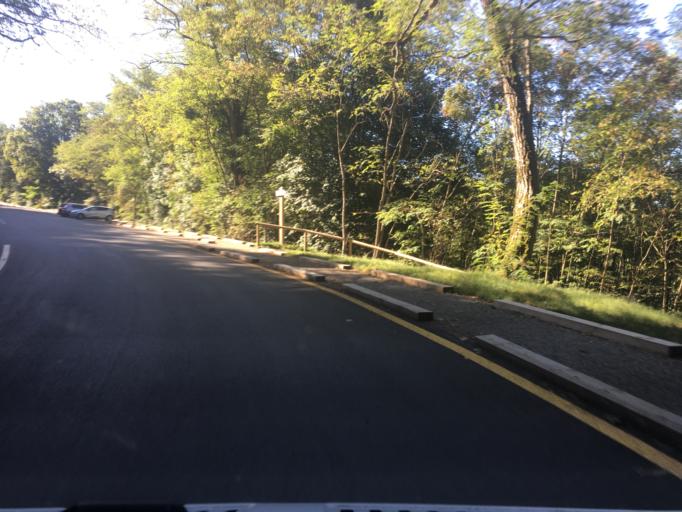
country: FR
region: Auvergne
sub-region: Departement du Cantal
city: Lanobre
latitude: 45.4437
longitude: 2.5076
